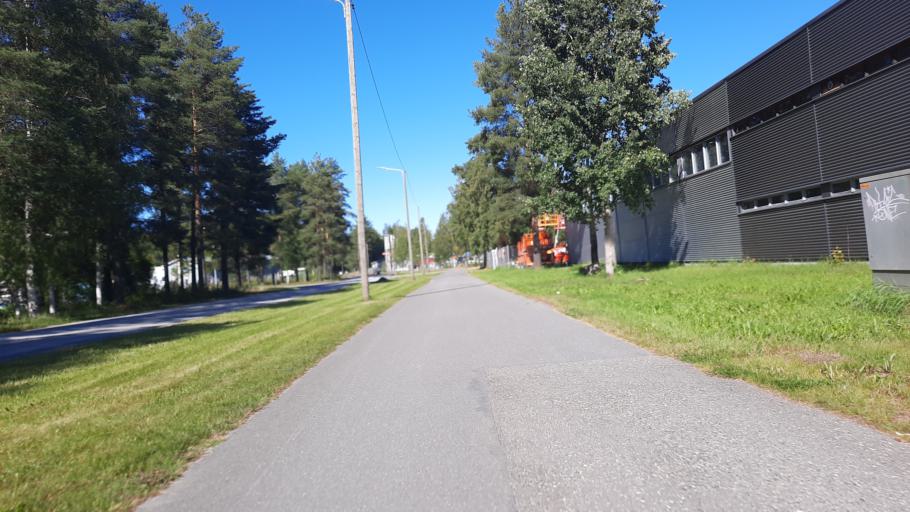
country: FI
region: North Karelia
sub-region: Joensuu
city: Joensuu
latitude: 62.6199
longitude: 29.7665
